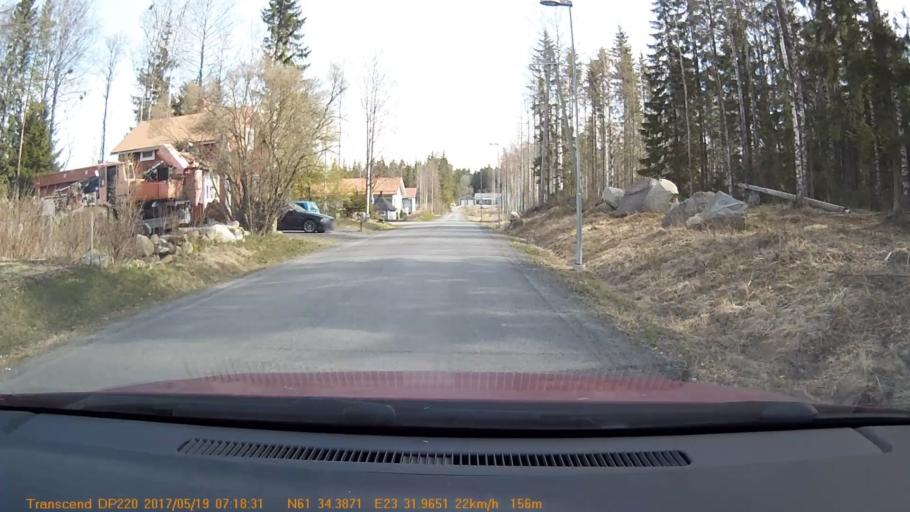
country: FI
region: Pirkanmaa
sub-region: Tampere
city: Yloejaervi
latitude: 61.5730
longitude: 23.5327
